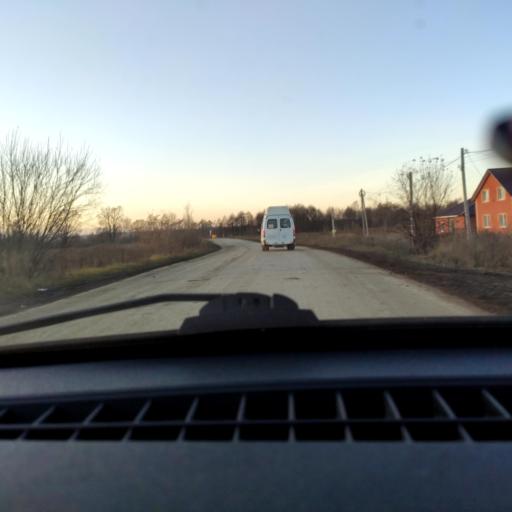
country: RU
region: Bashkortostan
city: Kabakovo
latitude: 54.6992
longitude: 56.1294
